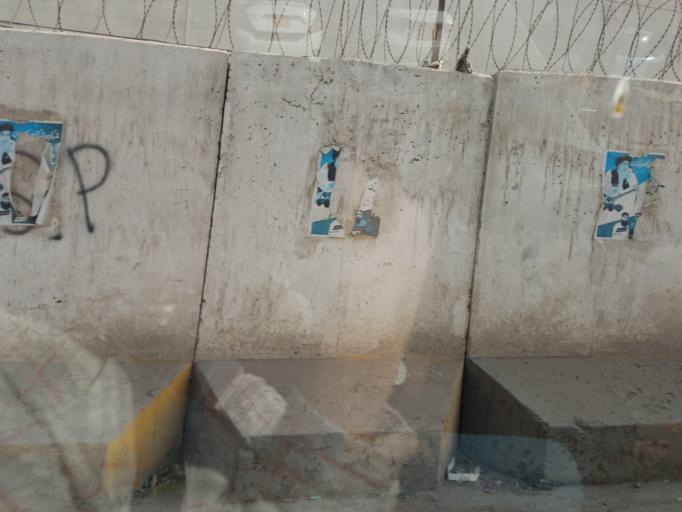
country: PK
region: Sindh
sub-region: Karachi District
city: Karachi
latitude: 24.8894
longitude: 67.0518
